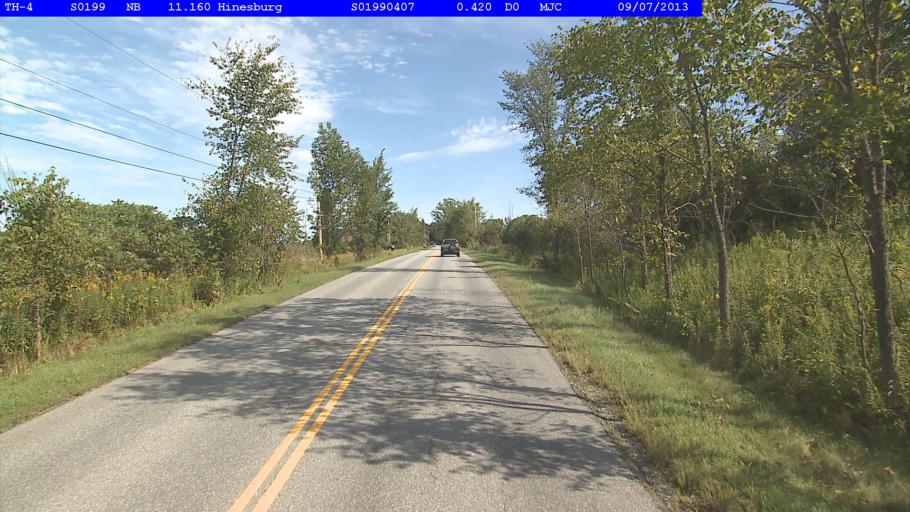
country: US
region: Vermont
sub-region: Chittenden County
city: Hinesburg
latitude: 44.2842
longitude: -73.1081
